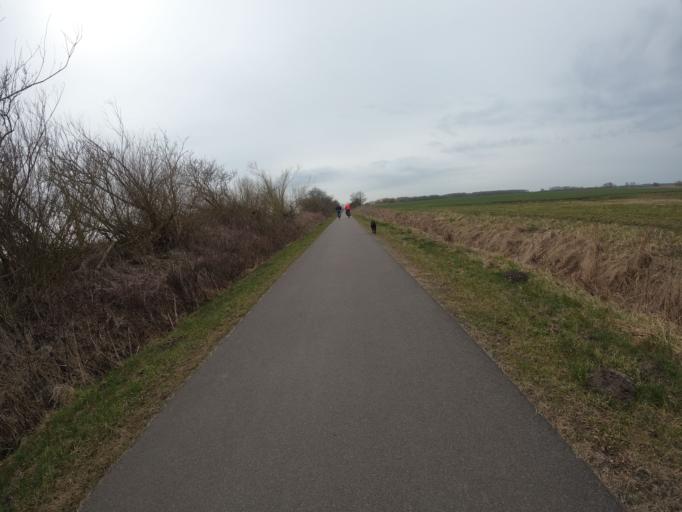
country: PL
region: West Pomeranian Voivodeship
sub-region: Powiat gryficki
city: Mrzezyno
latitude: 54.1162
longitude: 15.3029
